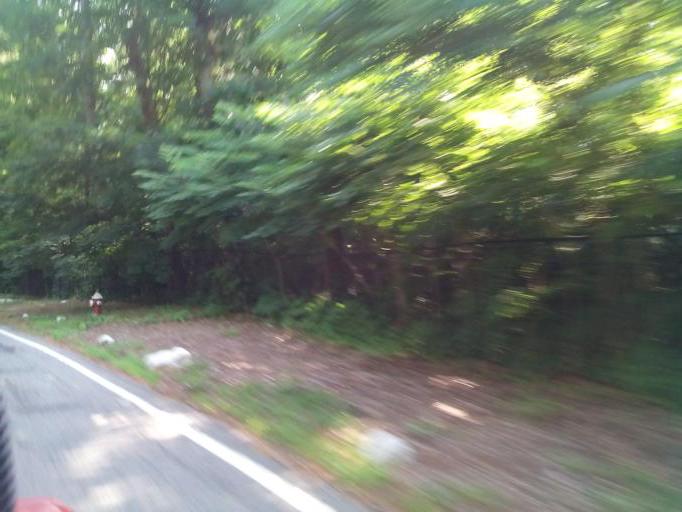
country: US
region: New York
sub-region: Nassau County
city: Upper Brookville
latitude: 40.8540
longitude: -73.5708
